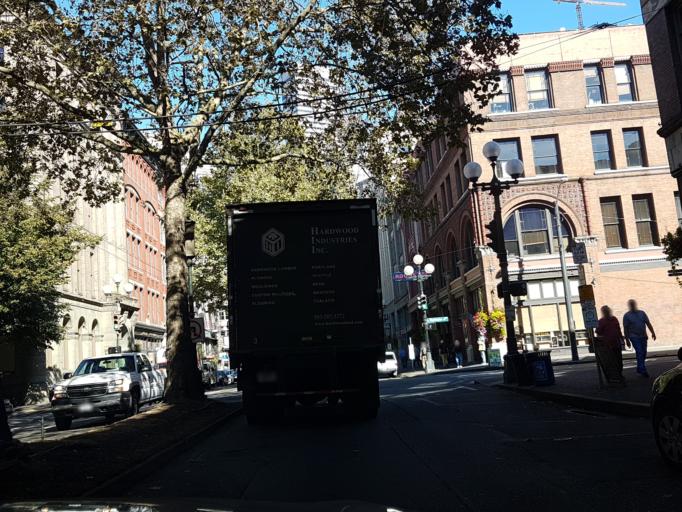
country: US
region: Washington
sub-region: King County
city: Seattle
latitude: 47.6006
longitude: -122.3342
